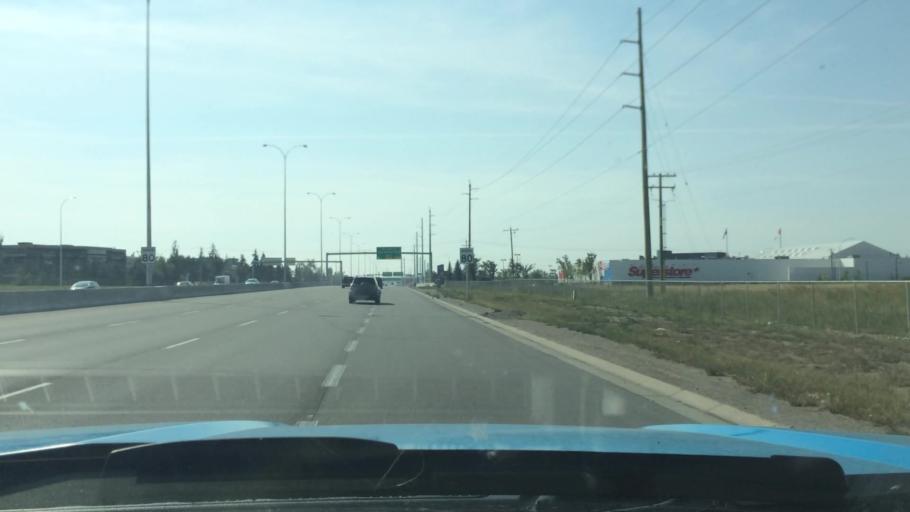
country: CA
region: Alberta
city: Calgary
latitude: 50.9129
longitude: -114.0674
